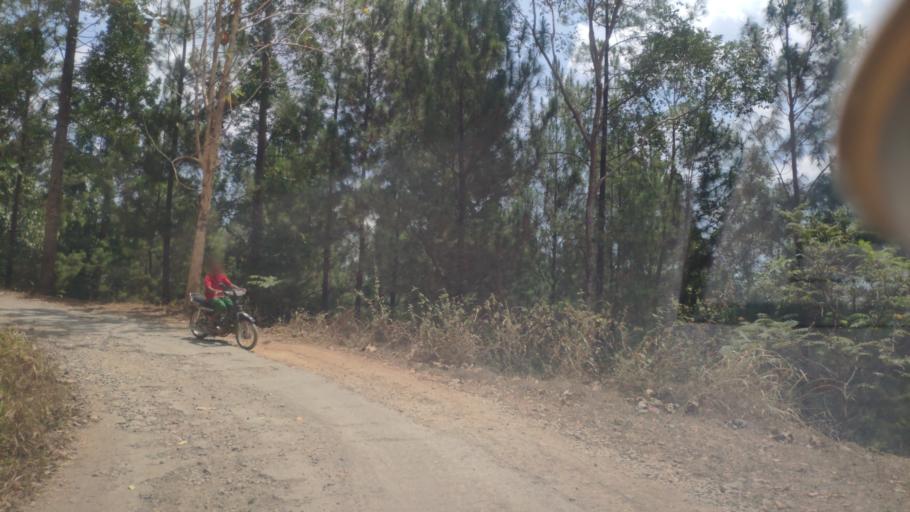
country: ID
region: Central Java
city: Gombong
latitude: -7.4796
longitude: 109.6126
